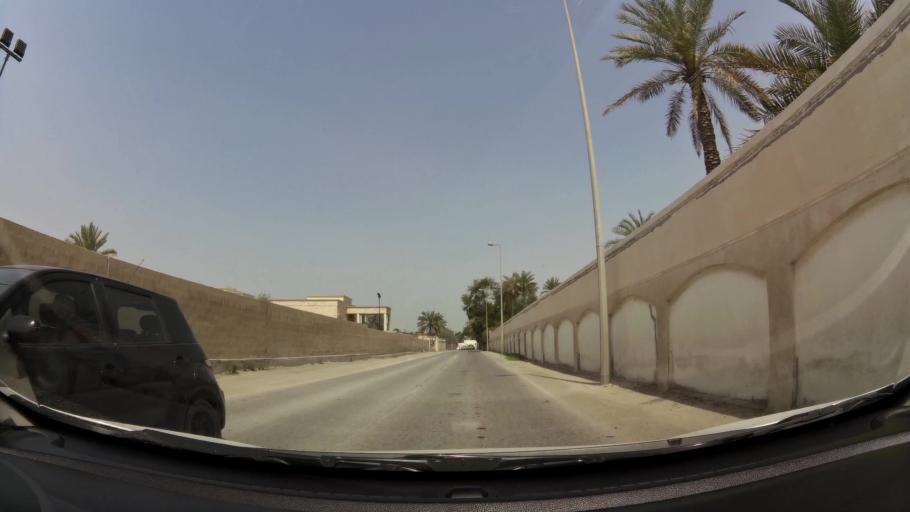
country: BH
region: Manama
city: Jidd Hafs
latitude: 26.2224
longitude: 50.4779
